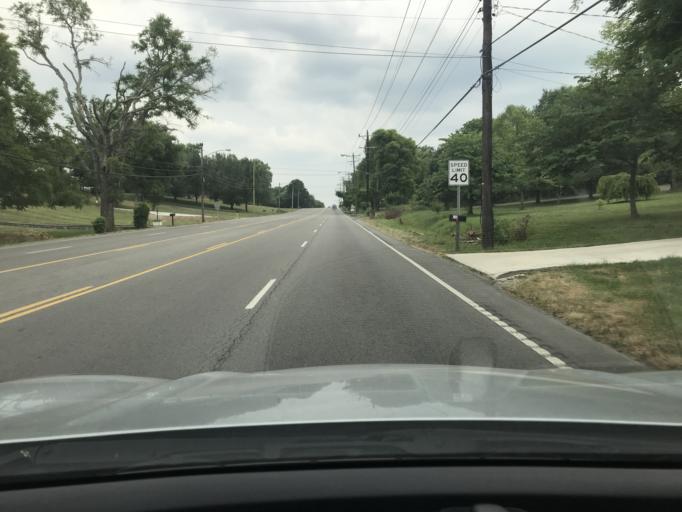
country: US
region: Tennessee
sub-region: Davidson County
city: Goodlettsville
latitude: 36.3123
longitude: -86.7151
